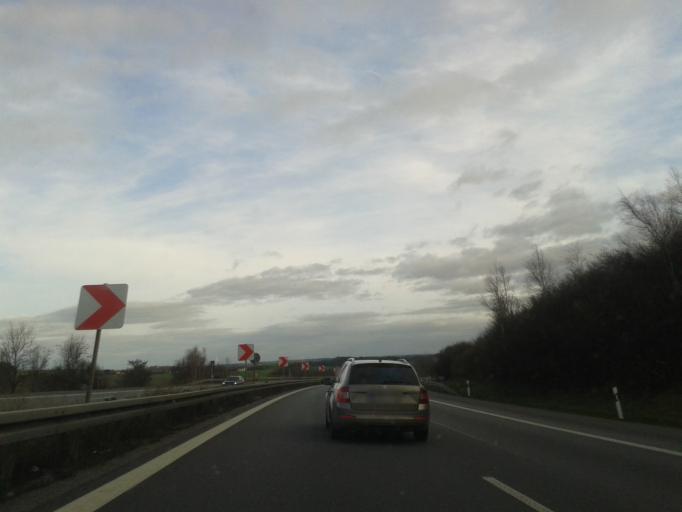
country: DE
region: Saxony
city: Rammenau
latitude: 51.1802
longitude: 14.1477
